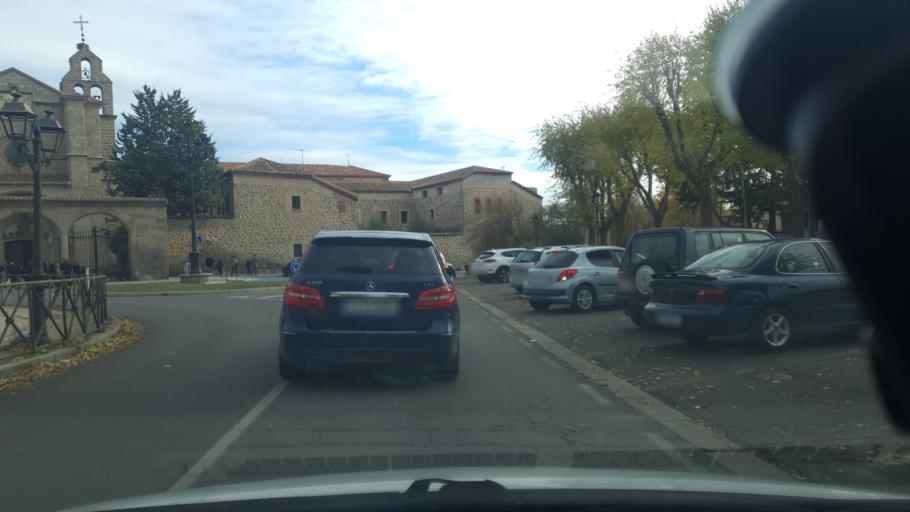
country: ES
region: Castille and Leon
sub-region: Provincia de Avila
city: Avila
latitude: 40.6505
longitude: -4.6905
